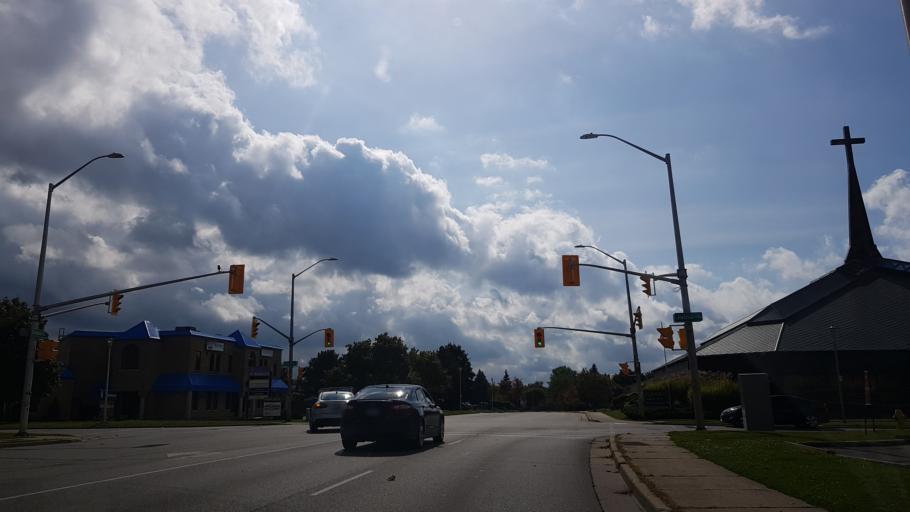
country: CA
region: Ontario
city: London
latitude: 42.9413
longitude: -81.2369
